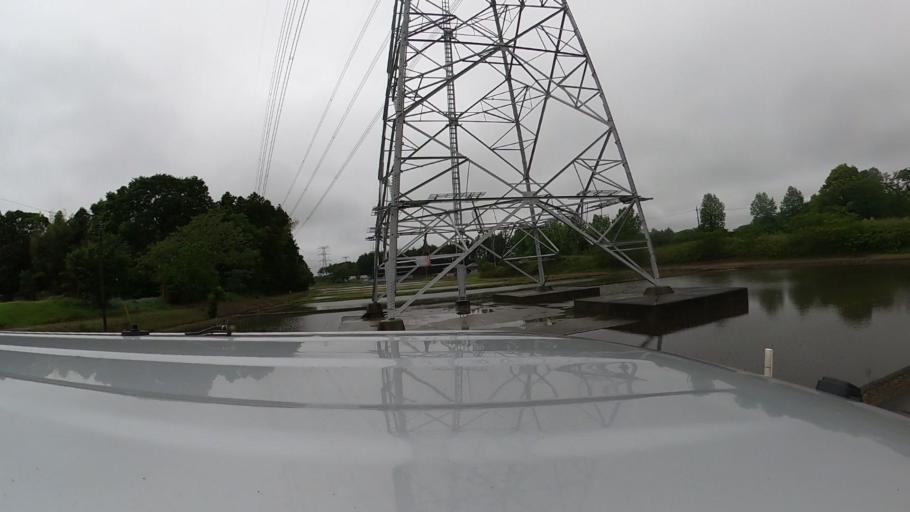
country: JP
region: Ibaraki
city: Ushiku
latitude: 36.0062
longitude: 140.1310
